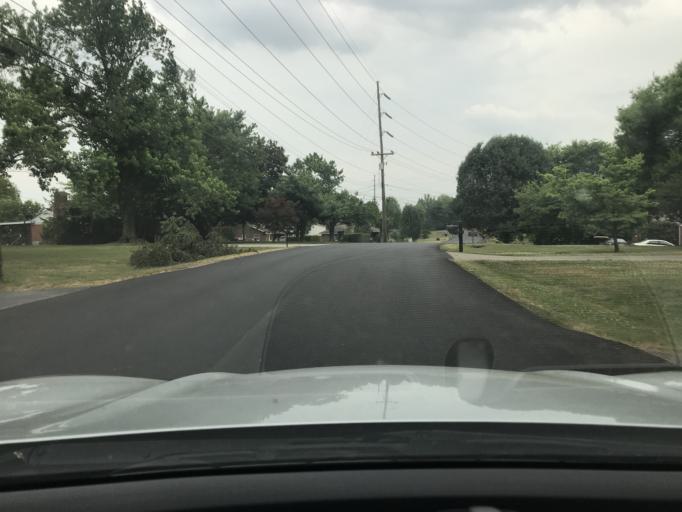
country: US
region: Tennessee
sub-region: Davidson County
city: Goodlettsville
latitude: 36.3000
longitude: -86.7140
